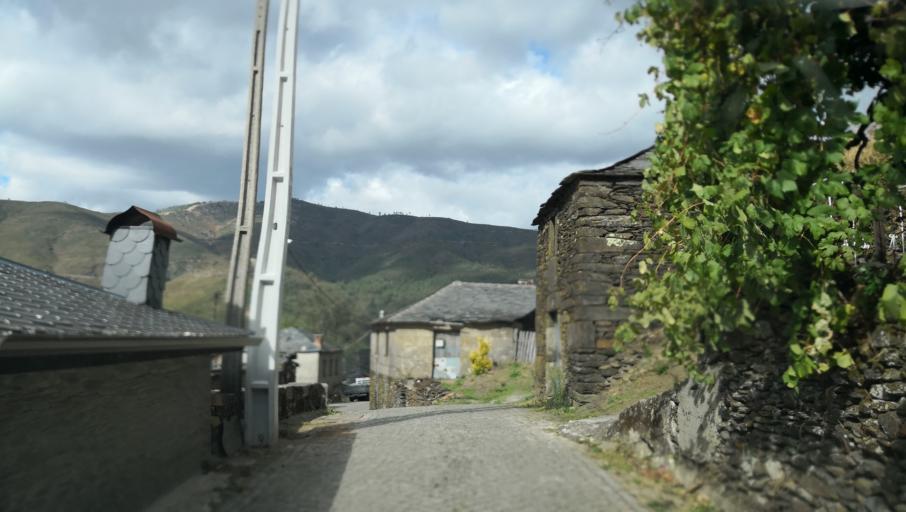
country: PT
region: Vila Real
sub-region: Mondim de Basto
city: Mondim de Basto
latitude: 41.3625
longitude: -7.8869
